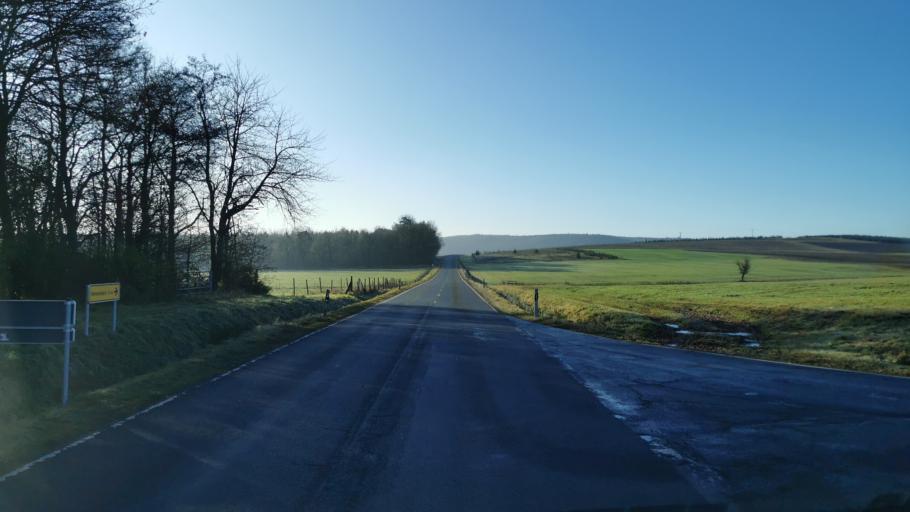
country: DE
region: Rheinland-Pfalz
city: Salm
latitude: 50.1481
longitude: 6.7020
